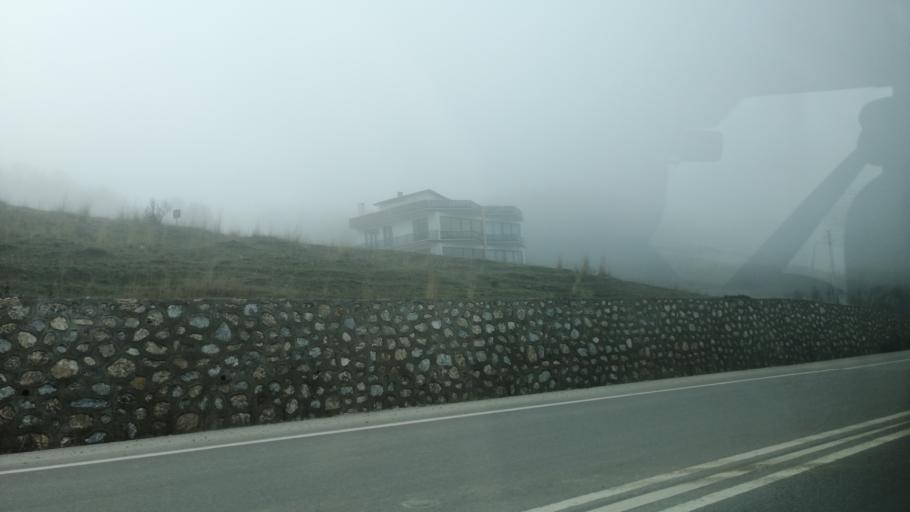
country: TR
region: Yalova
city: Kadikoy
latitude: 40.6498
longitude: 29.2062
